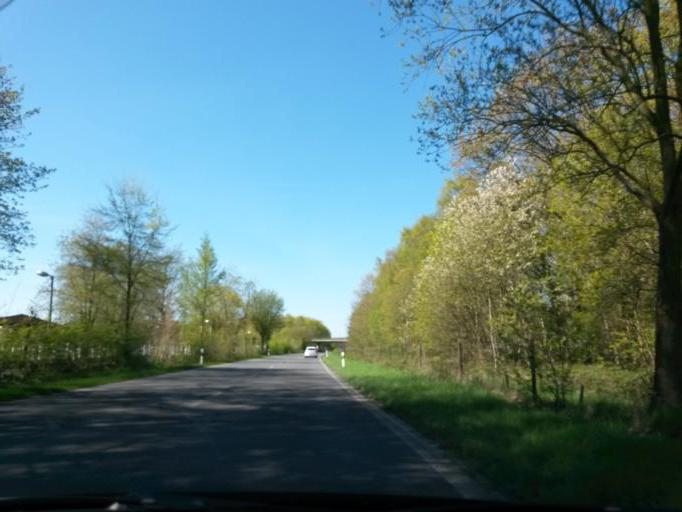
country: DE
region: Schleswig-Holstein
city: Pinneberg
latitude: 53.6269
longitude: 9.7780
